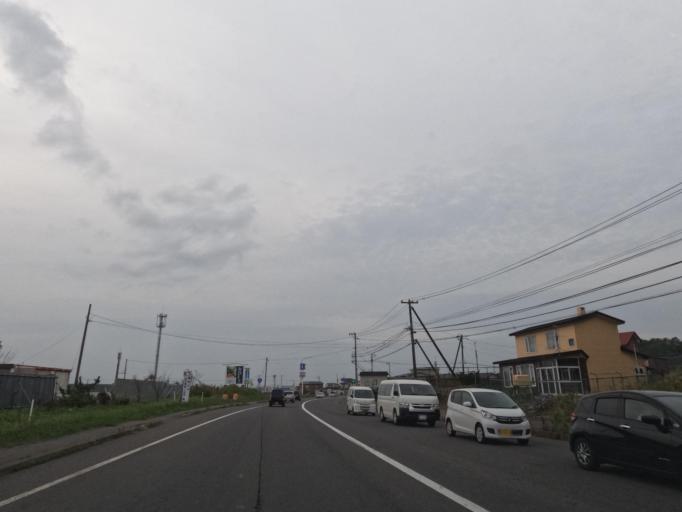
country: JP
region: Hokkaido
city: Date
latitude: 42.3839
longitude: 140.9119
